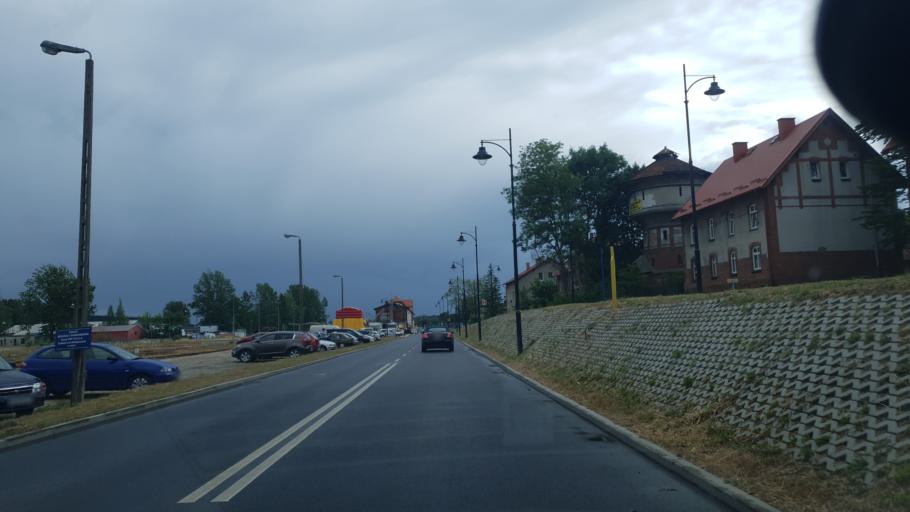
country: PL
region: Pomeranian Voivodeship
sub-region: Powiat kartuski
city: Kartuzy
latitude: 54.3366
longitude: 18.2071
